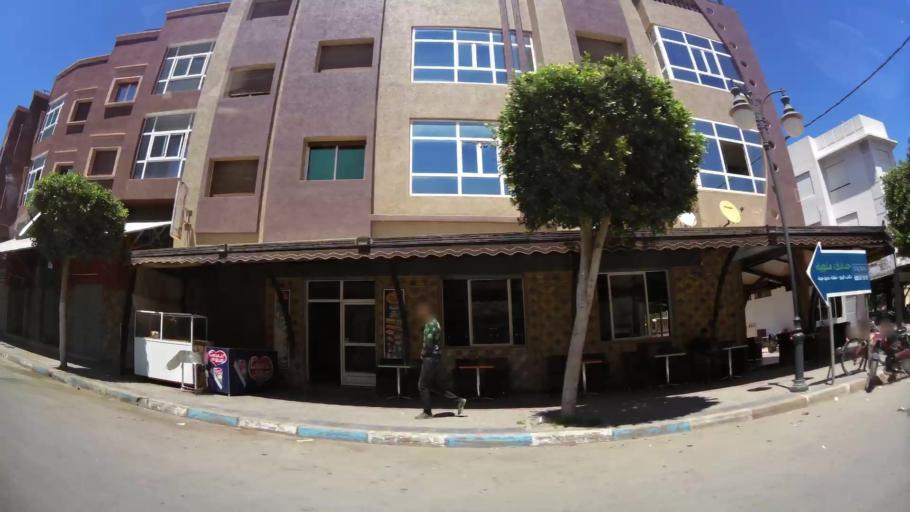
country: MA
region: Oriental
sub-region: Berkane-Taourirt
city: Madagh
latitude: 35.0785
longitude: -2.2259
